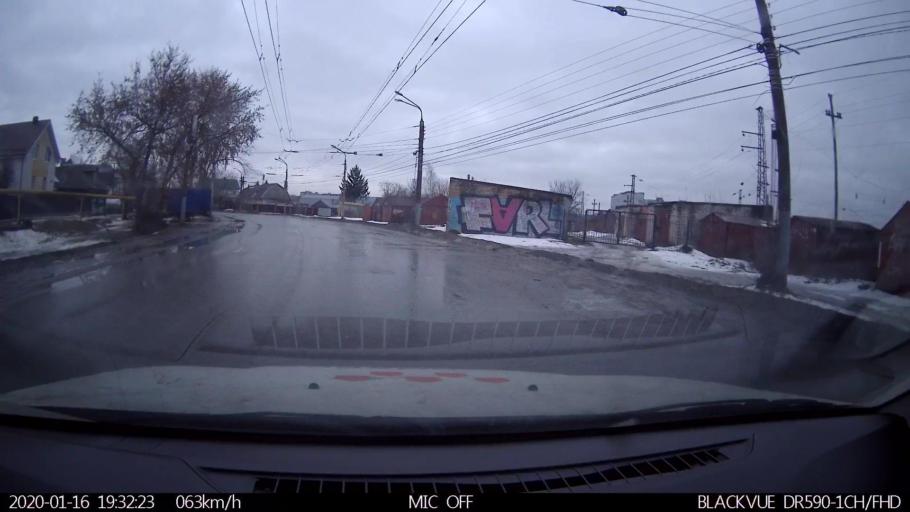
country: RU
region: Nizjnij Novgorod
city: Gorbatovka
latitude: 56.3637
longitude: 43.8340
